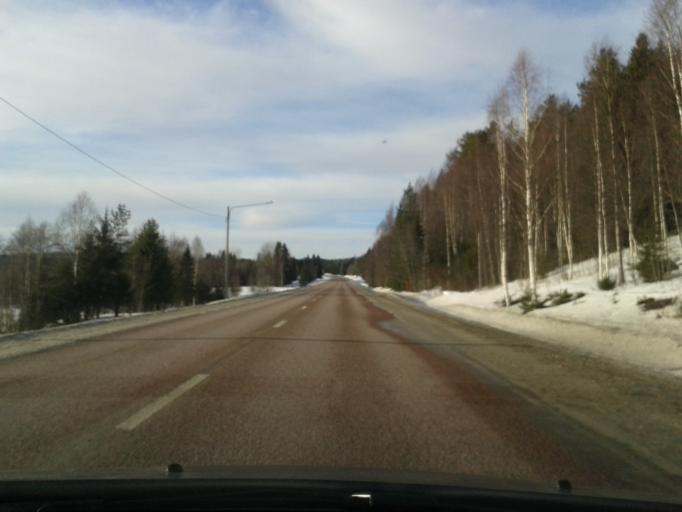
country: SE
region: Vaesternorrland
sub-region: OErnskoeldsviks Kommun
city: Bredbyn
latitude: 63.3921
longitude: 18.3385
